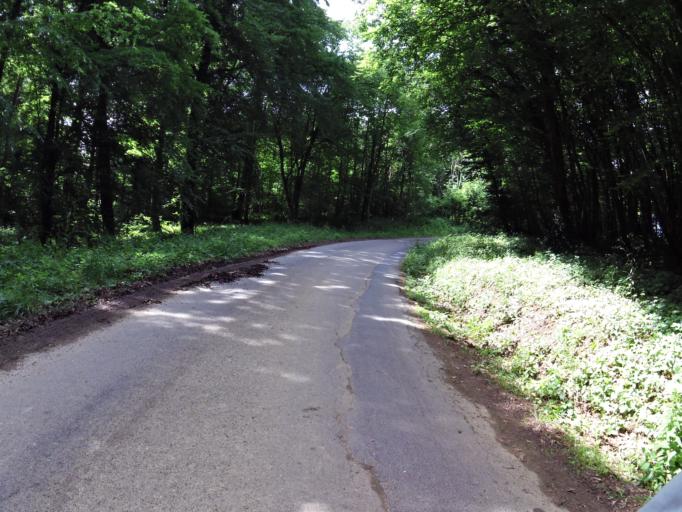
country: FR
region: Lorraine
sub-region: Departement de la Meuse
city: Stenay
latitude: 49.5374
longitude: 5.1462
